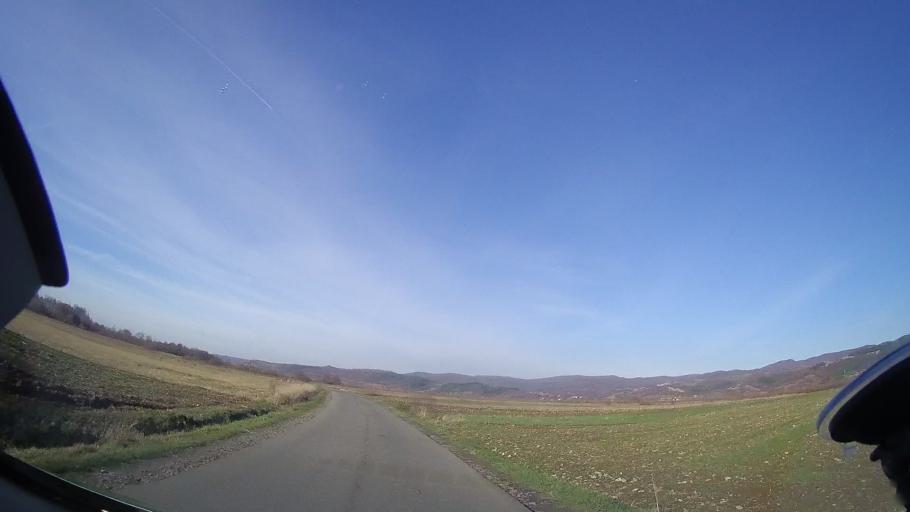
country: RO
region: Bihor
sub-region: Comuna Auseu
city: Auseu
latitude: 47.0279
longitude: 22.4840
